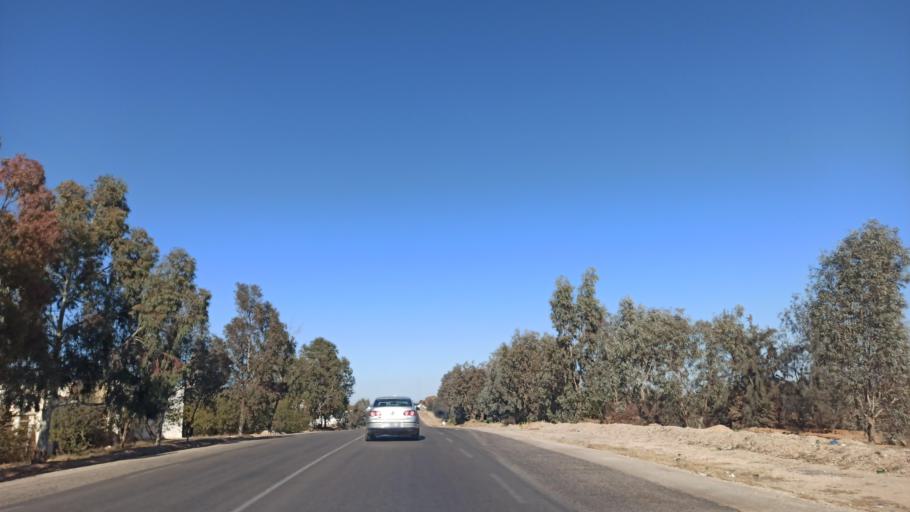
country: TN
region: Sidi Bu Zayd
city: Jilma
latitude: 35.1400
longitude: 9.3613
